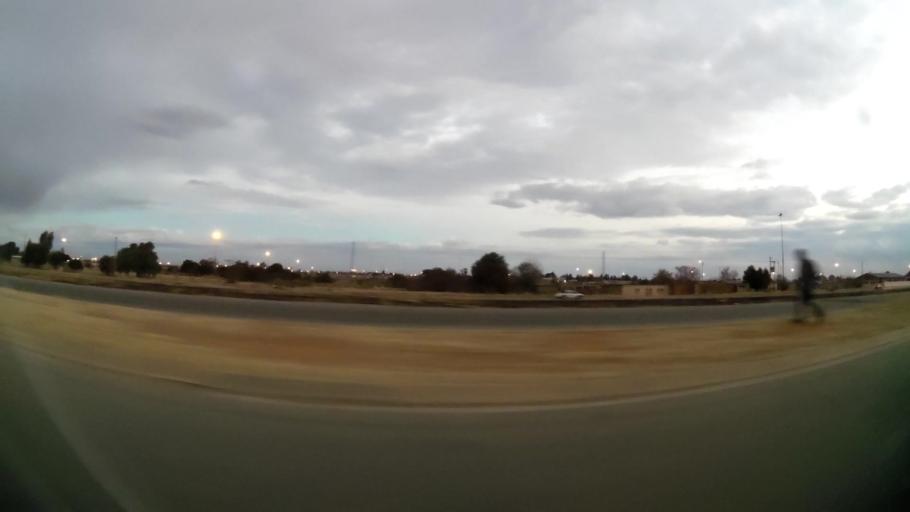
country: ZA
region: Orange Free State
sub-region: Lejweleputswa District Municipality
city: Welkom
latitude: -27.9541
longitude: 26.7873
